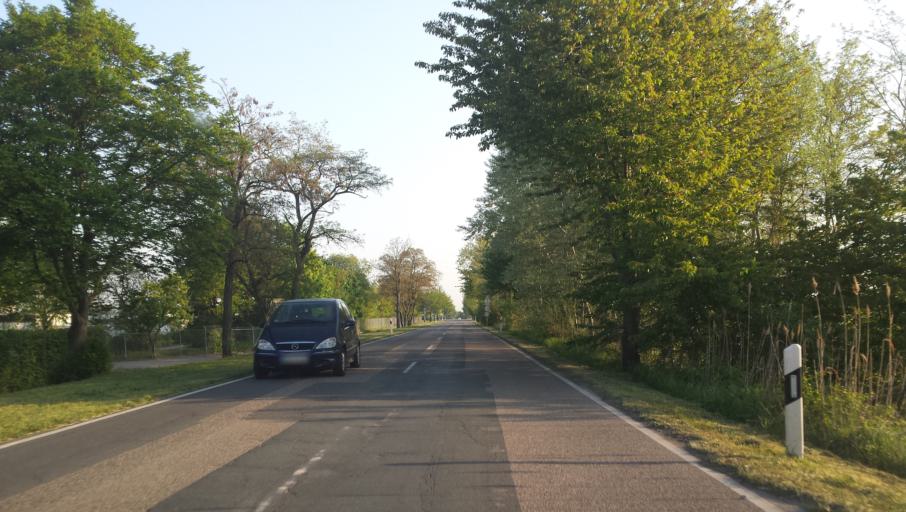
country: DE
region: Baden-Wuerttemberg
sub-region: Karlsruhe Region
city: Ketsch
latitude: 49.3819
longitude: 8.5272
